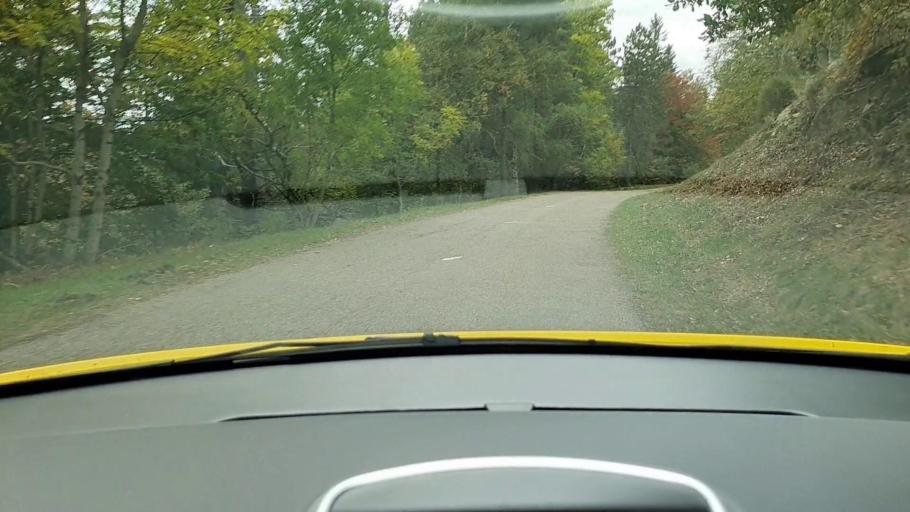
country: FR
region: Languedoc-Roussillon
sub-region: Departement de la Lozere
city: Meyrueis
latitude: 44.0988
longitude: 3.4694
